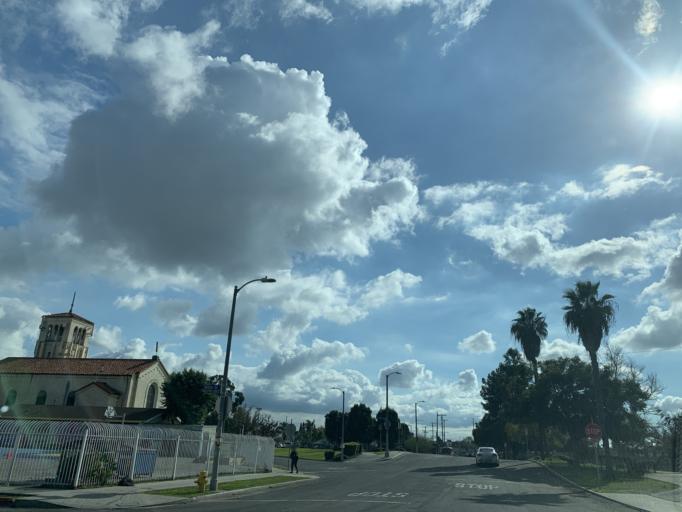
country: US
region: California
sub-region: Los Angeles County
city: Willowbrook
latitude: 33.9408
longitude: -118.2427
